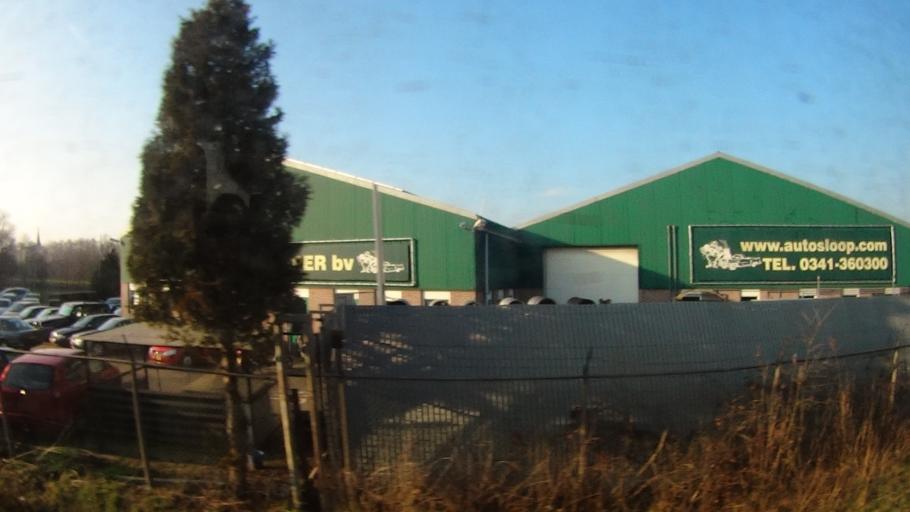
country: NL
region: Gelderland
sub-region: Gemeente Putten
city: Putten
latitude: 52.2480
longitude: 5.5510
